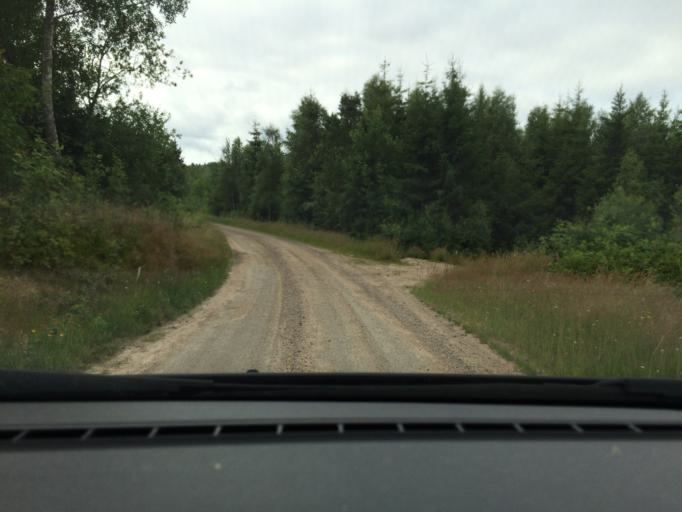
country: SE
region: Joenkoeping
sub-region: Varnamo Kommun
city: Forsheda
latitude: 57.0576
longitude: 13.7868
